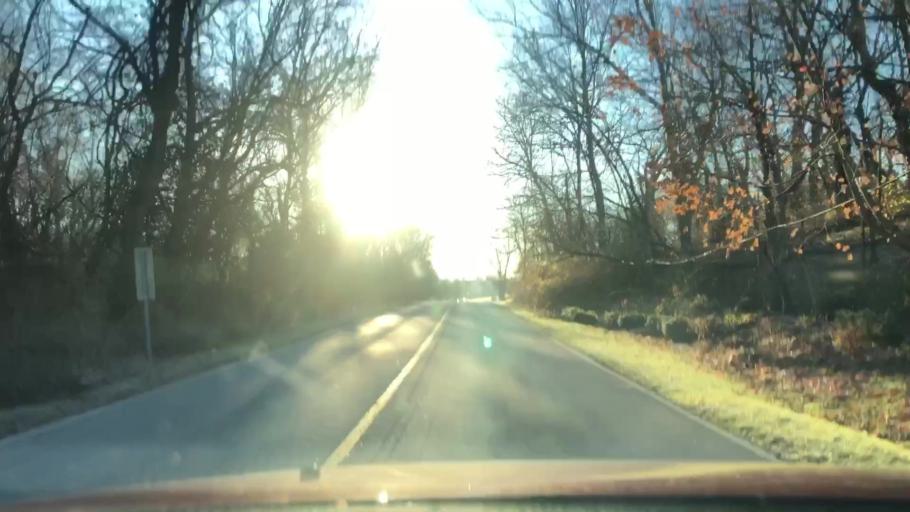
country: US
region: Missouri
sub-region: Greene County
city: Springfield
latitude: 37.1616
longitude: -93.2442
